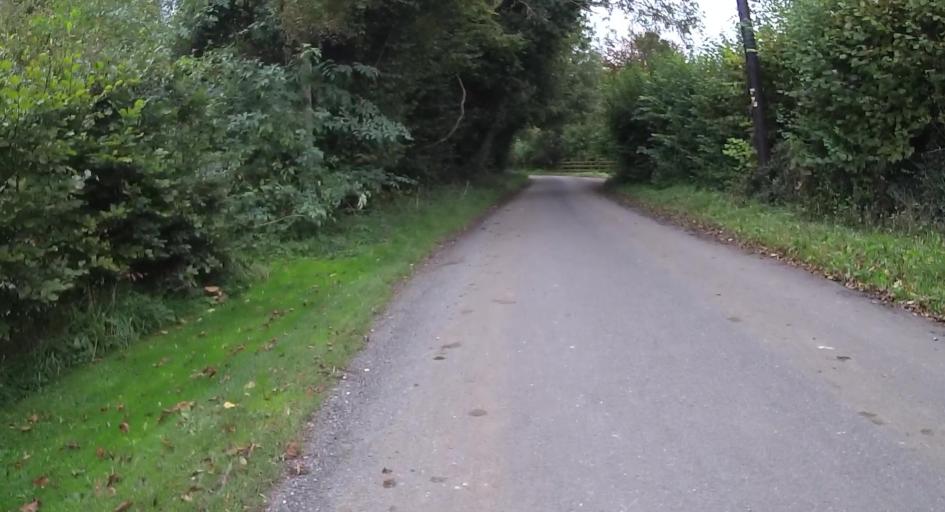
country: GB
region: England
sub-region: Hampshire
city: Four Marks
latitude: 51.1110
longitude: -1.0782
